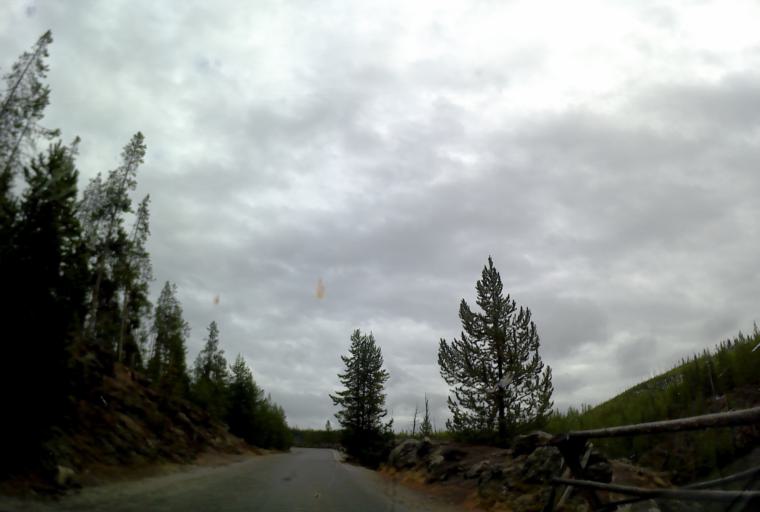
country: US
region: Montana
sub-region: Gallatin County
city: West Yellowstone
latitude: 44.6622
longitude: -111.1036
